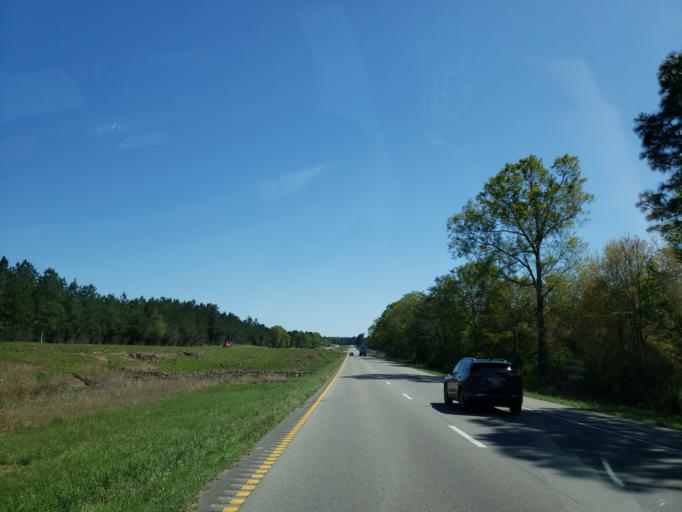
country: US
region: Mississippi
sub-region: Stone County
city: Wiggins
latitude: 30.9985
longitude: -89.2015
